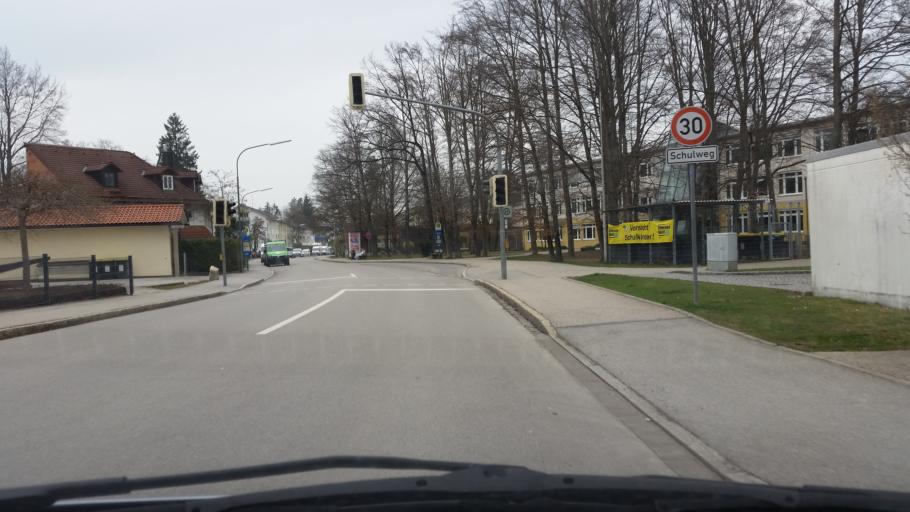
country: DE
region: Bavaria
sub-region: Upper Bavaria
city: Geretsried
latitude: 47.8559
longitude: 11.4806
